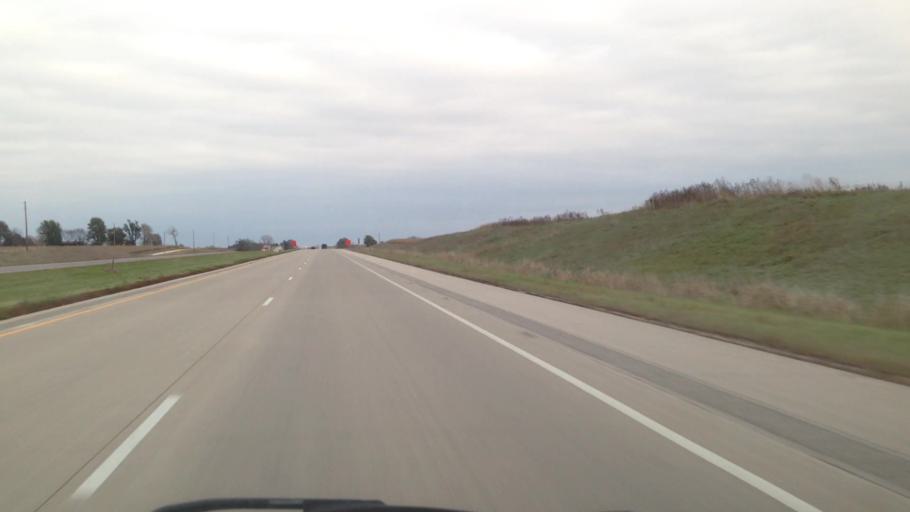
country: US
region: Minnesota
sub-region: Winona County
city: Lewiston
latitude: 43.9325
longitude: -91.9153
